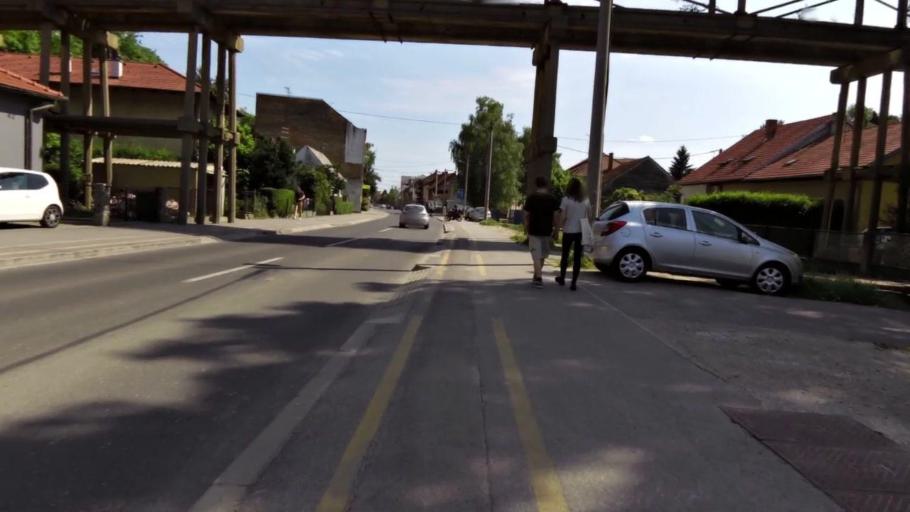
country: HR
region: Grad Zagreb
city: Jankomir
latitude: 45.8163
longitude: 15.9267
